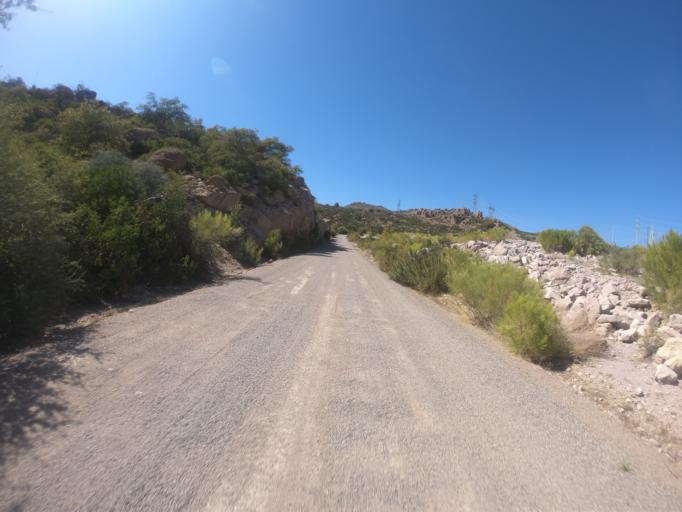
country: US
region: Arizona
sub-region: Pinal County
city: Superior
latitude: 33.3357
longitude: -111.0388
